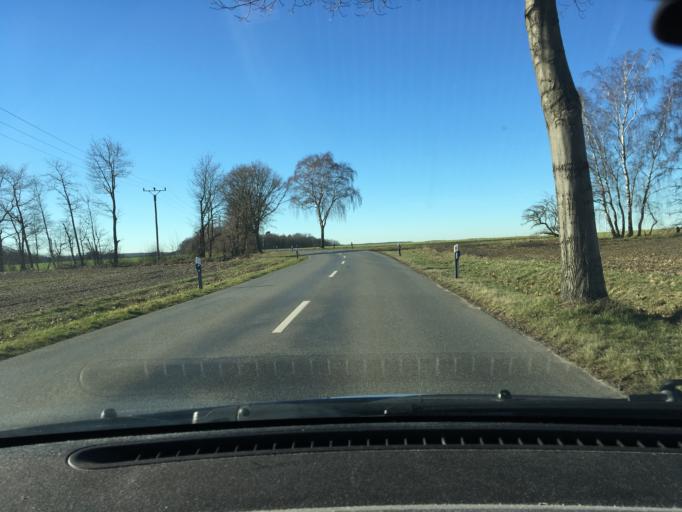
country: DE
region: Lower Saxony
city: Hanstedt Eins
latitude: 53.0236
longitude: 10.3722
